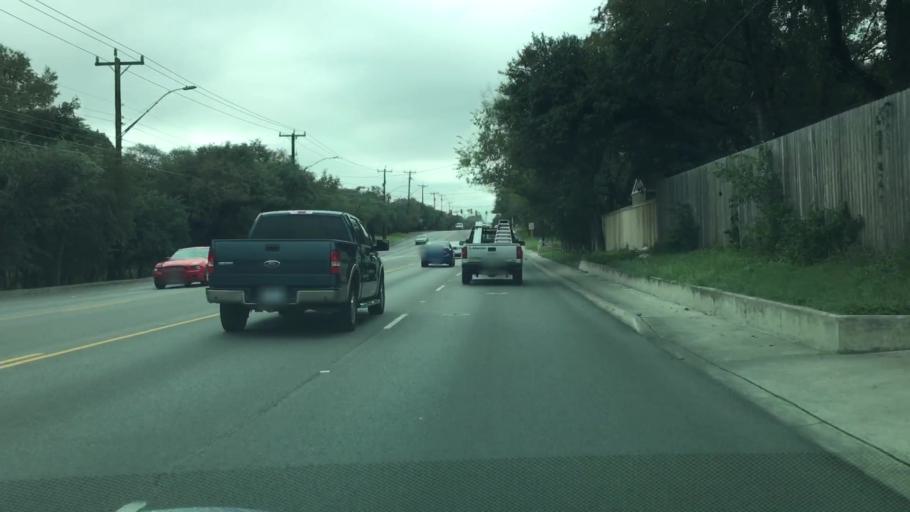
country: US
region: Texas
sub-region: Bexar County
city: Hollywood Park
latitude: 29.5642
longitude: -98.4564
